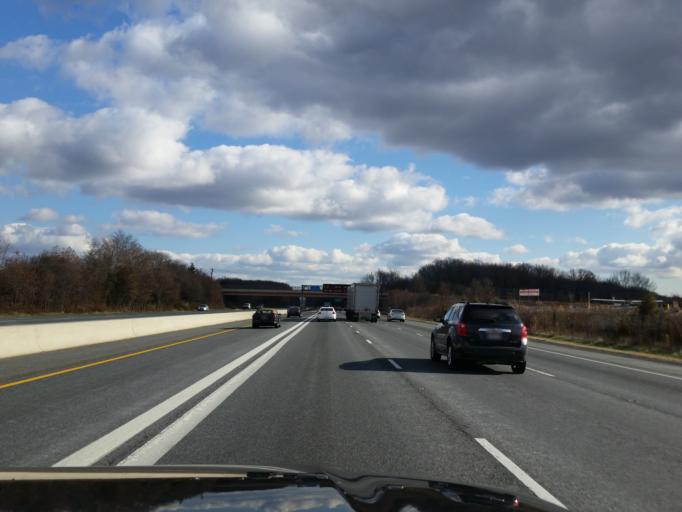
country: US
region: Maryland
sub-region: Prince George's County
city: Mitchellville
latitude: 38.9449
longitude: -76.7737
